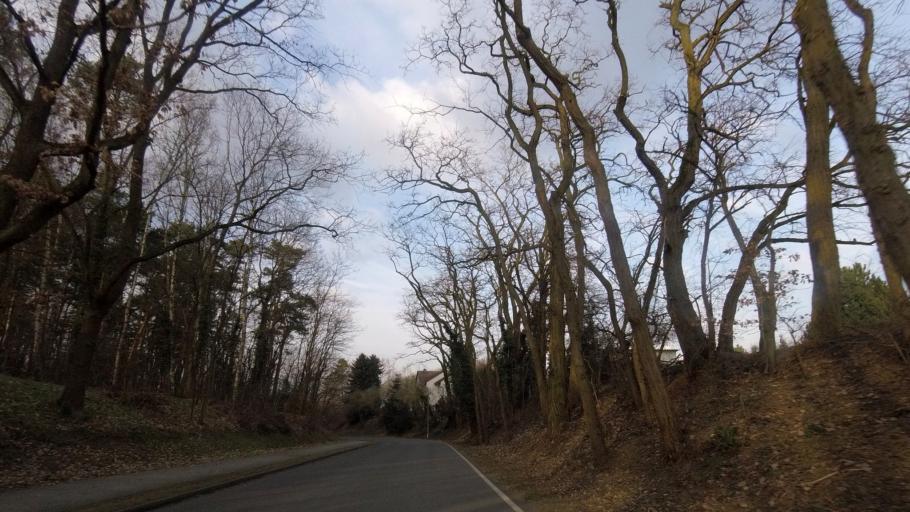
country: DE
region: Brandenburg
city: Belzig
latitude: 52.1328
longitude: 12.5865
